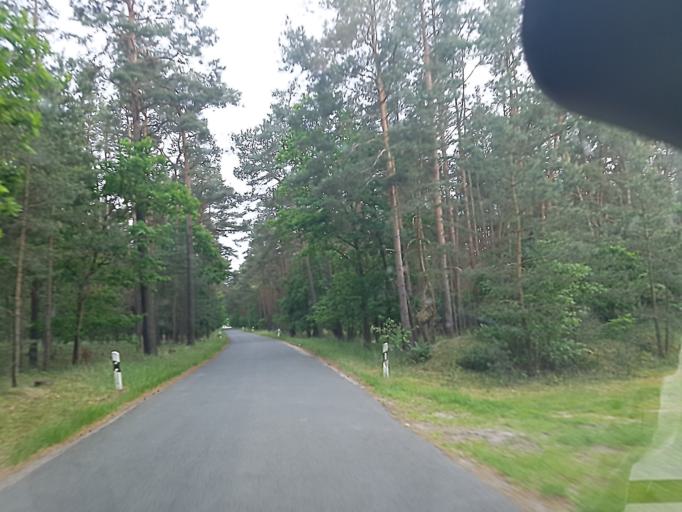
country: DE
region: Saxony-Anhalt
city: Holzdorf
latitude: 51.7700
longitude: 13.1091
